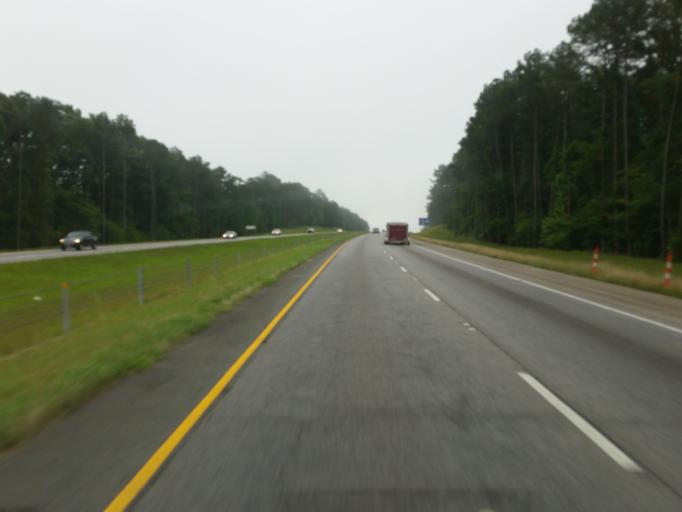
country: US
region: Louisiana
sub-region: Webster Parish
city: Minden
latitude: 32.5933
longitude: -93.3088
